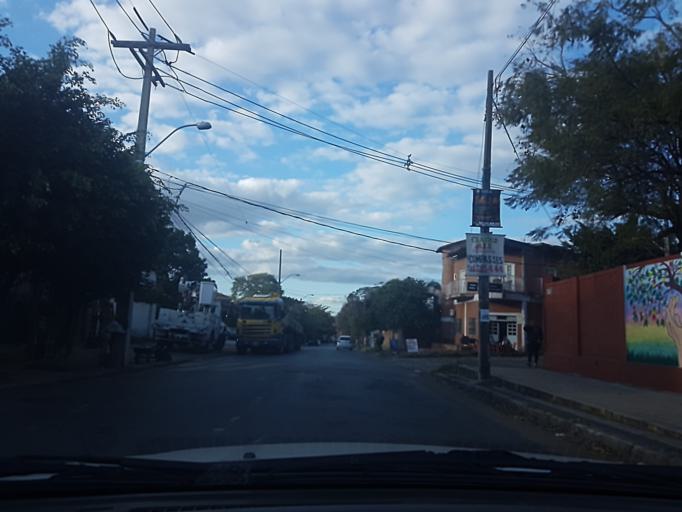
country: PY
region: Asuncion
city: Asuncion
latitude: -25.2650
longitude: -57.5815
